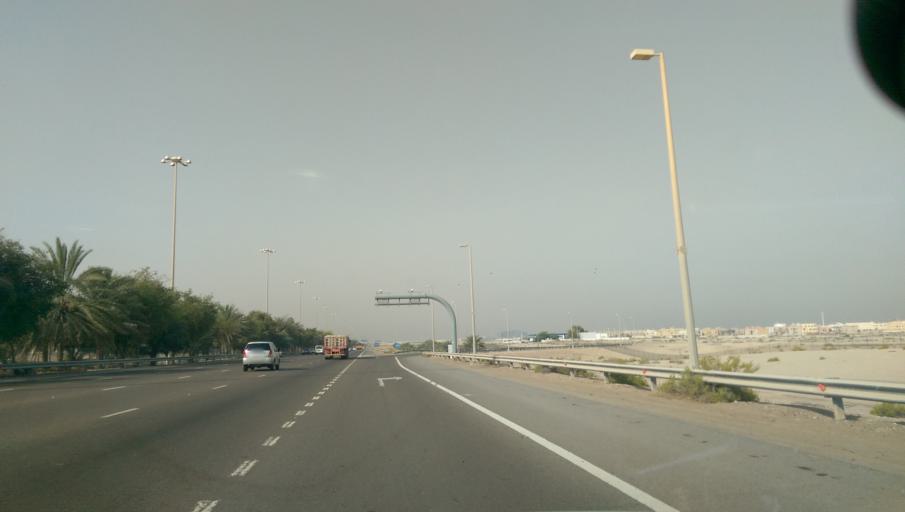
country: AE
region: Abu Dhabi
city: Abu Dhabi
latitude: 24.3588
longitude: 54.6482
